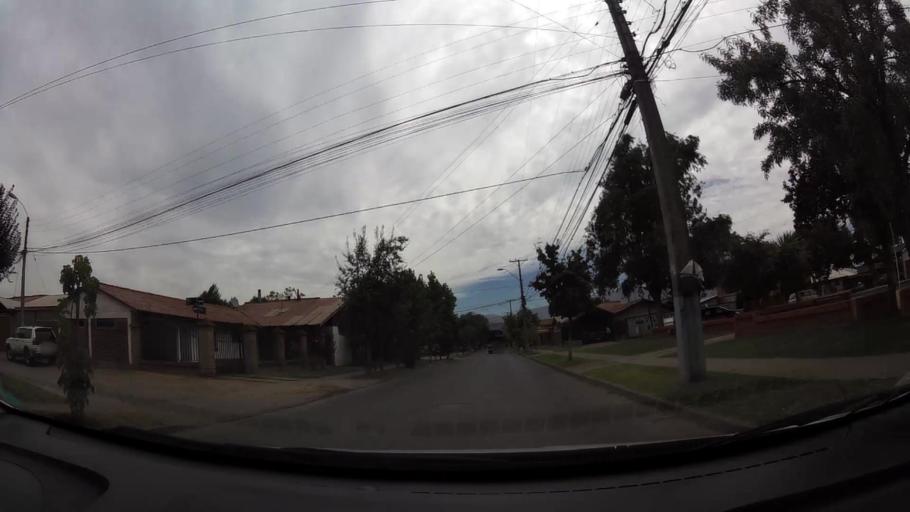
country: CL
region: O'Higgins
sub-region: Provincia de Cachapoal
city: Rancagua
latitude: -34.1353
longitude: -70.7329
